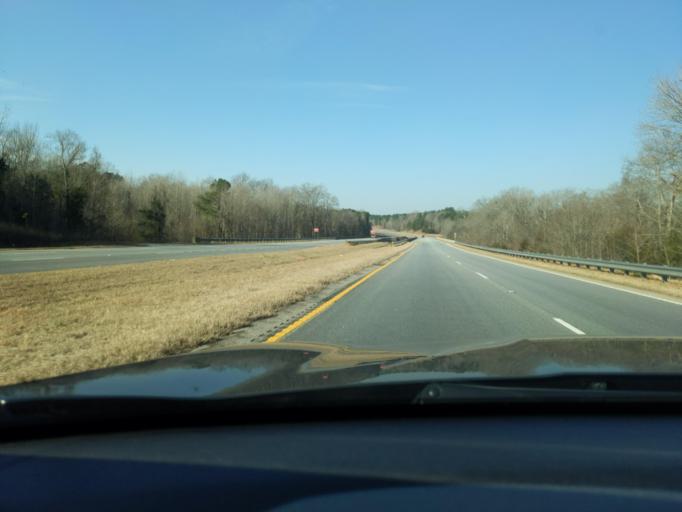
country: US
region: South Carolina
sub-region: Abbeville County
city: Calhoun Falls
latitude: 34.1107
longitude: -82.5080
